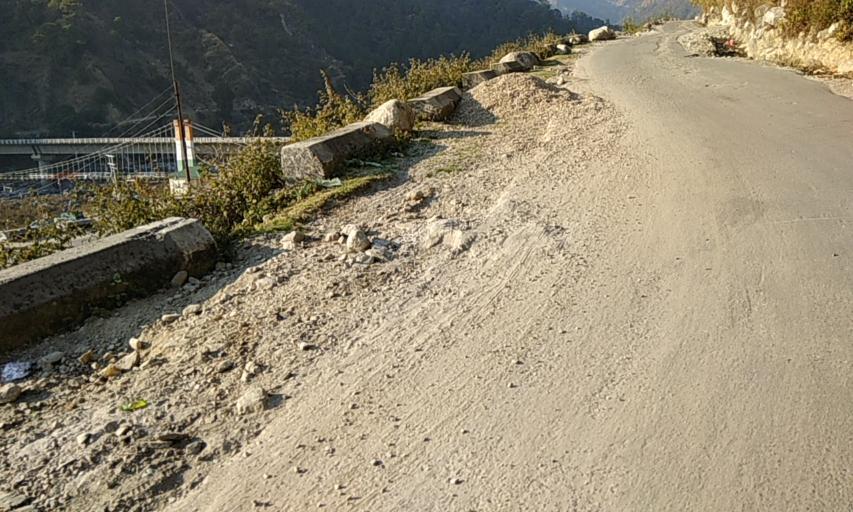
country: IN
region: Himachal Pradesh
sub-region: Kangra
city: Palampur
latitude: 32.1329
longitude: 76.5356
